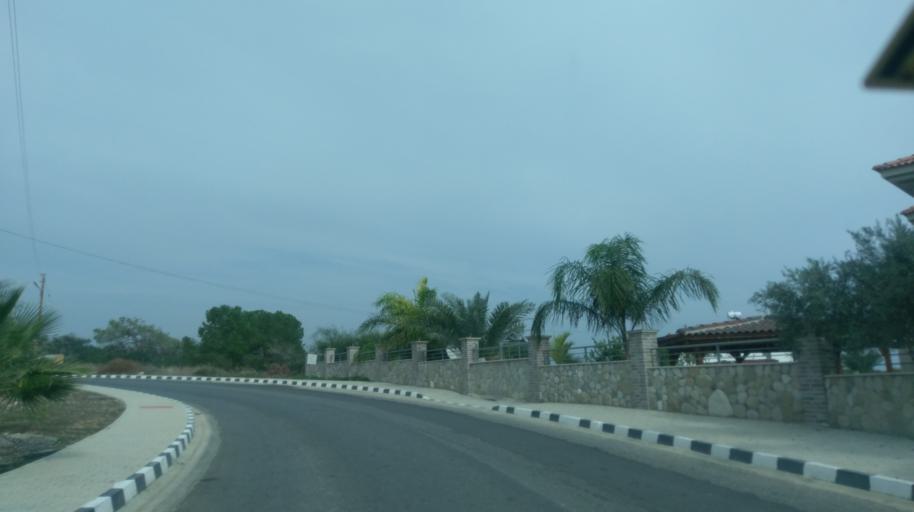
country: CY
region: Ammochostos
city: Trikomo
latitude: 35.3101
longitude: 33.9475
